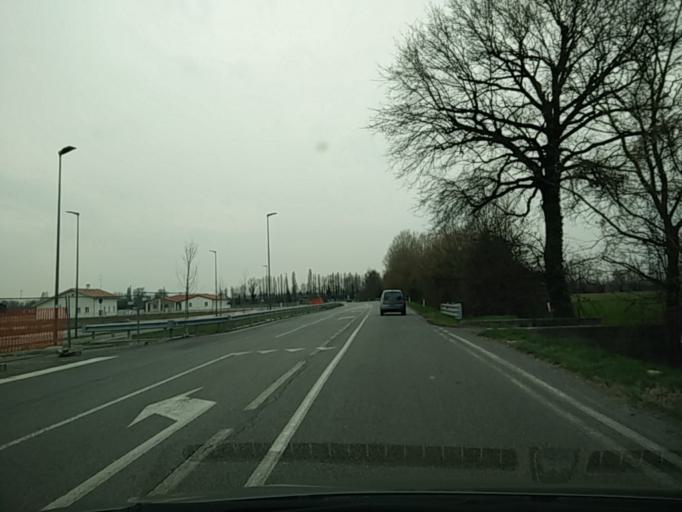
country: IT
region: Veneto
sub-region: Provincia di Venezia
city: Noale
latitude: 45.5607
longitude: 12.0699
